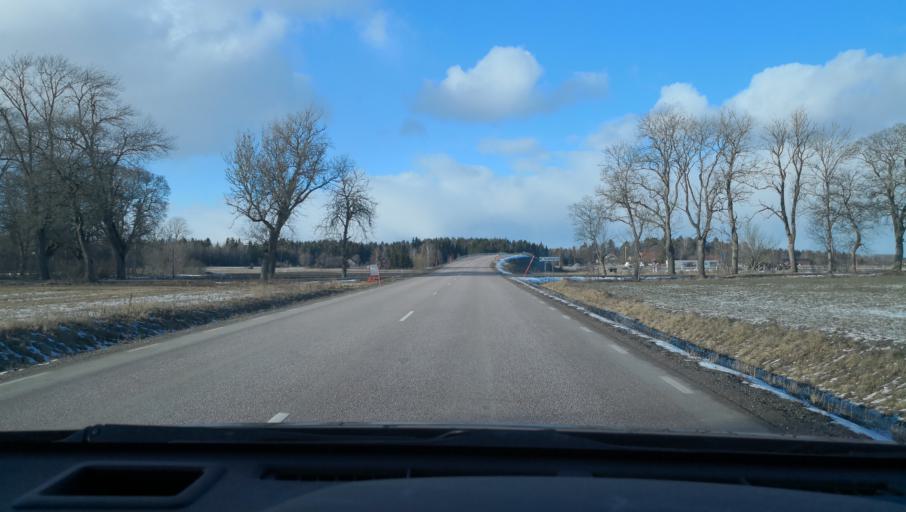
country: SE
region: Uppsala
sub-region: Enkopings Kommun
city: Hummelsta
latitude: 59.6417
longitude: 16.9672
